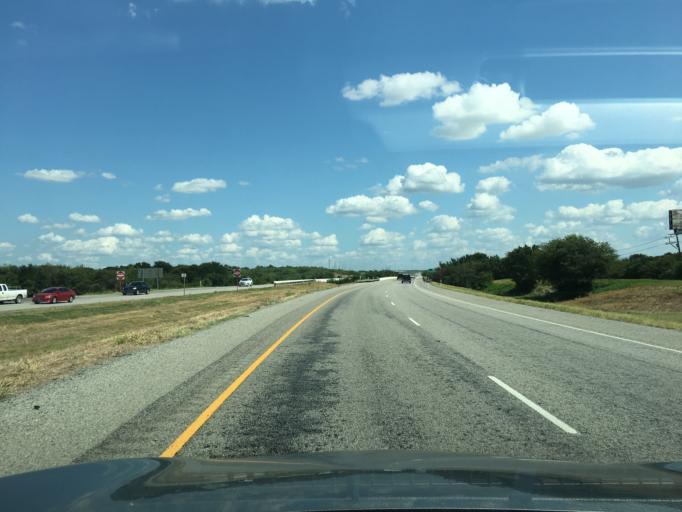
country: US
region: Texas
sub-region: Ellis County
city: Midlothian
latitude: 32.5145
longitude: -97.0699
